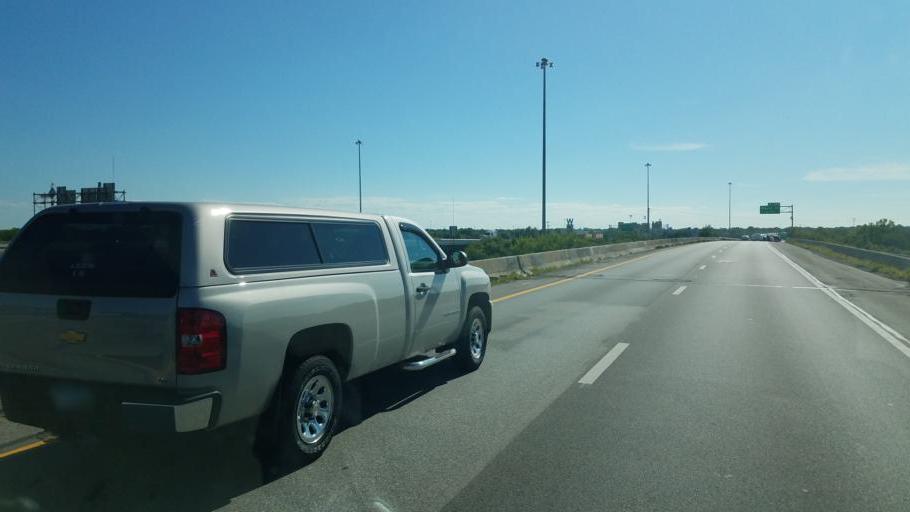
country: US
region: Ohio
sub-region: Franklin County
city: Columbus
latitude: 39.9514
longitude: -83.0157
